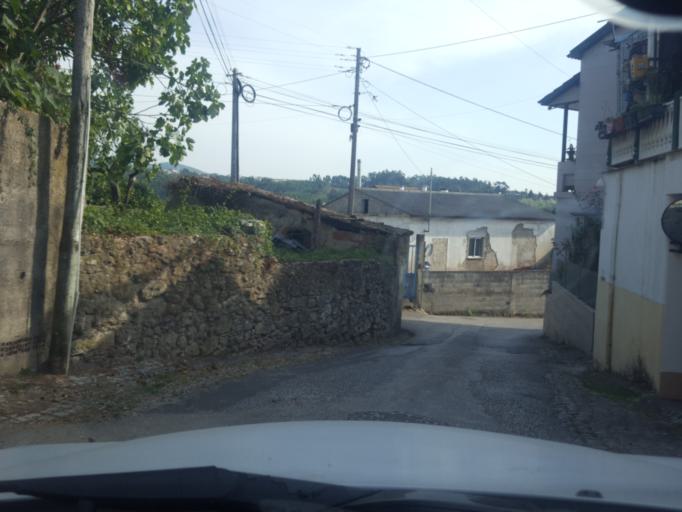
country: PT
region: Leiria
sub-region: Leiria
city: Leiria
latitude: 39.7217
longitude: -8.7806
